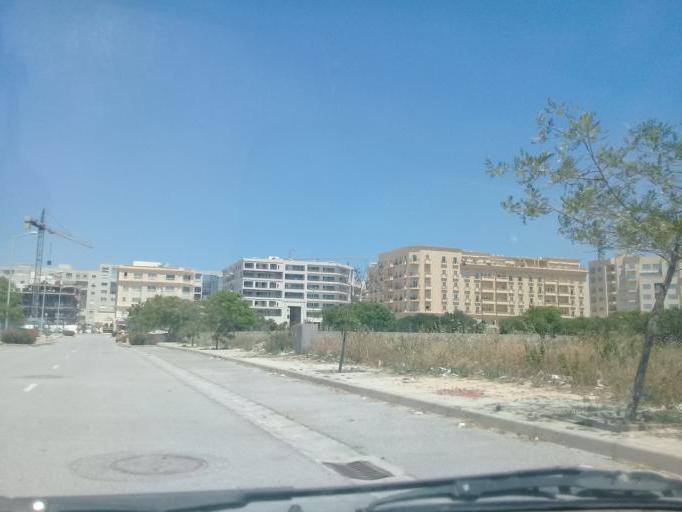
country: TN
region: Tunis
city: La Goulette
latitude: 36.8419
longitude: 10.2811
